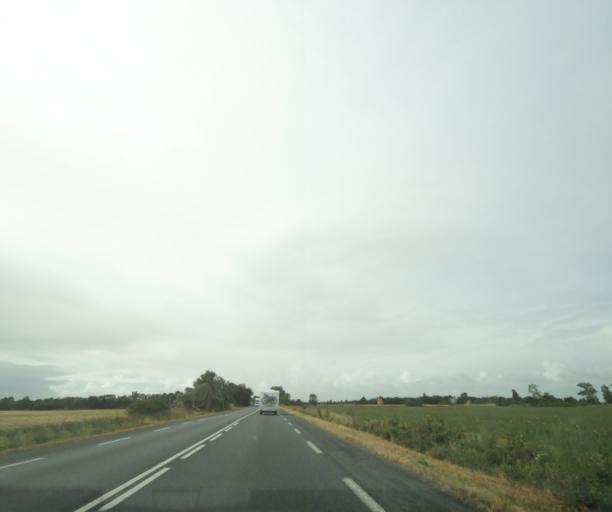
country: FR
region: Pays de la Loire
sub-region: Departement de la Vendee
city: Sainte-Gemme-la-Plaine
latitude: 46.4366
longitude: -1.0996
